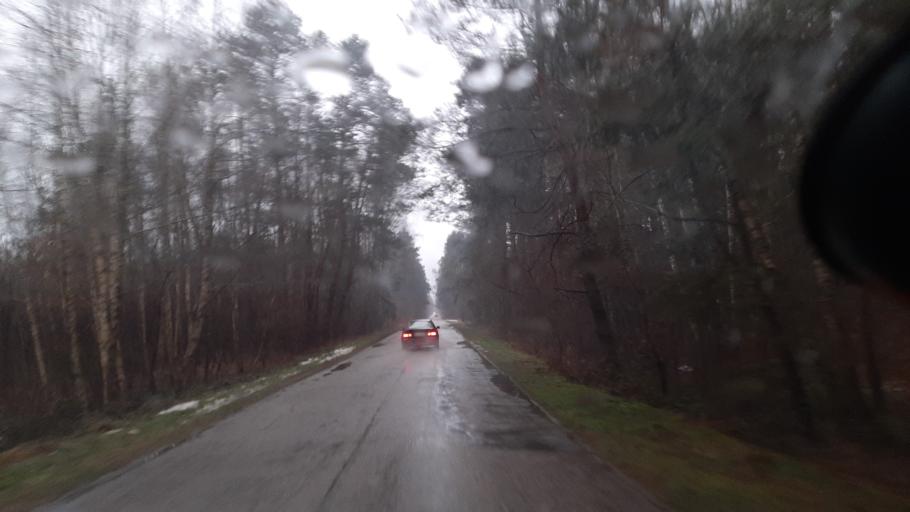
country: PL
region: Lublin Voivodeship
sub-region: Powiat lubartowski
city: Kamionka
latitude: 51.5079
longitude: 22.4898
